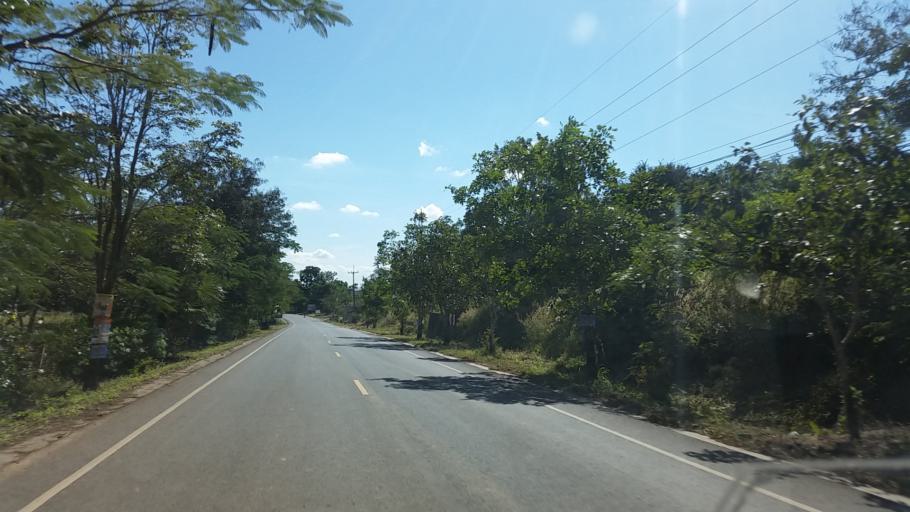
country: TH
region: Chaiyaphum
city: Thep Sathit
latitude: 15.5949
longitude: 101.4055
